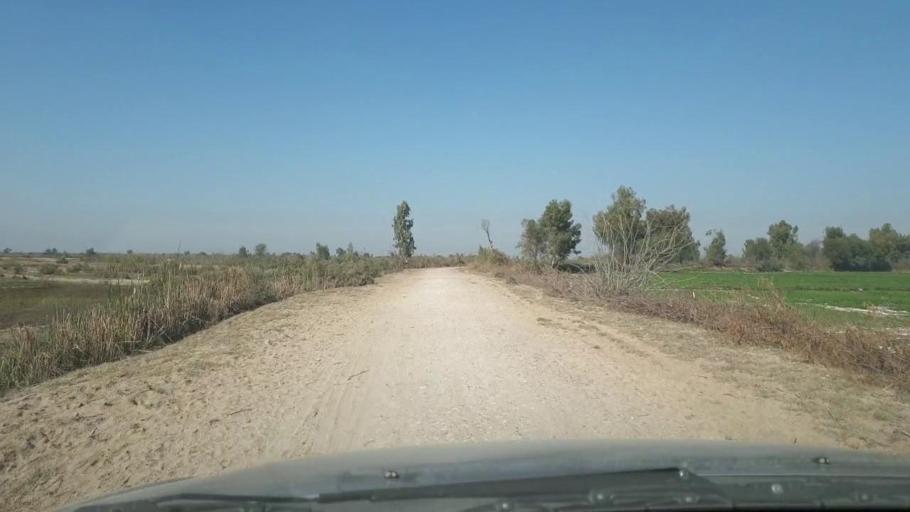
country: PK
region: Sindh
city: Adilpur
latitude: 27.8958
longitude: 69.2549
